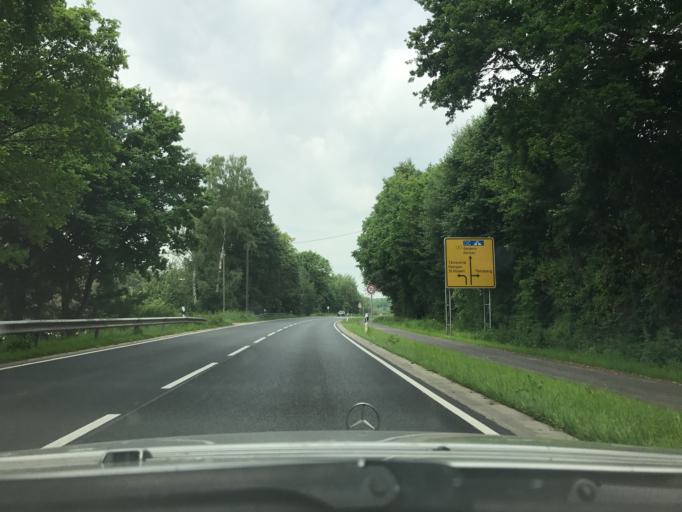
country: DE
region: North Rhine-Westphalia
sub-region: Regierungsbezirk Dusseldorf
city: Rheurdt
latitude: 51.4079
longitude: 6.4869
